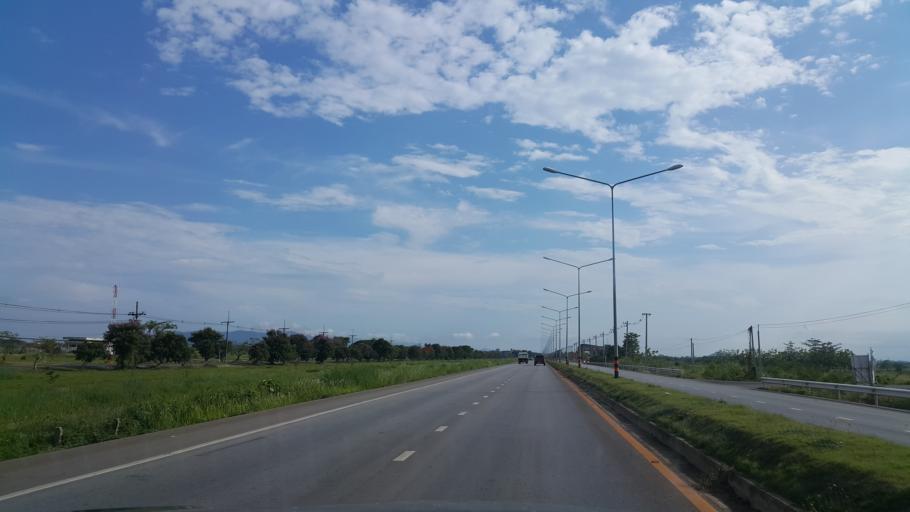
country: TH
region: Chiang Rai
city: Chiang Rai
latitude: 19.9472
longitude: 99.8725
